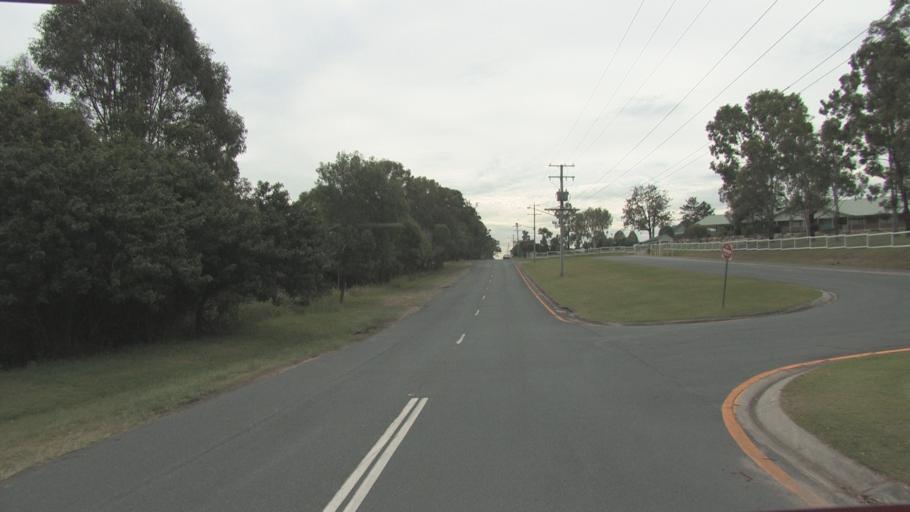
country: AU
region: Queensland
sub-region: Logan
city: Waterford West
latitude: -27.7094
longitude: 153.1481
